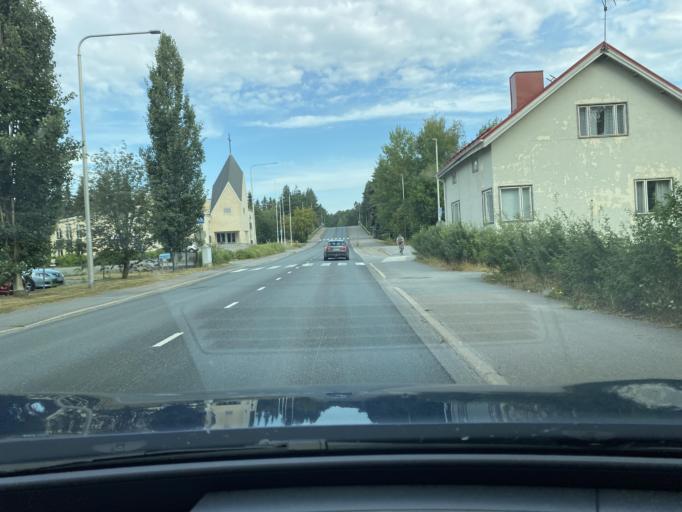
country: FI
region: Pirkanmaa
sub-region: Lounais-Pirkanmaa
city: Vammala
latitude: 61.3488
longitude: 22.8999
